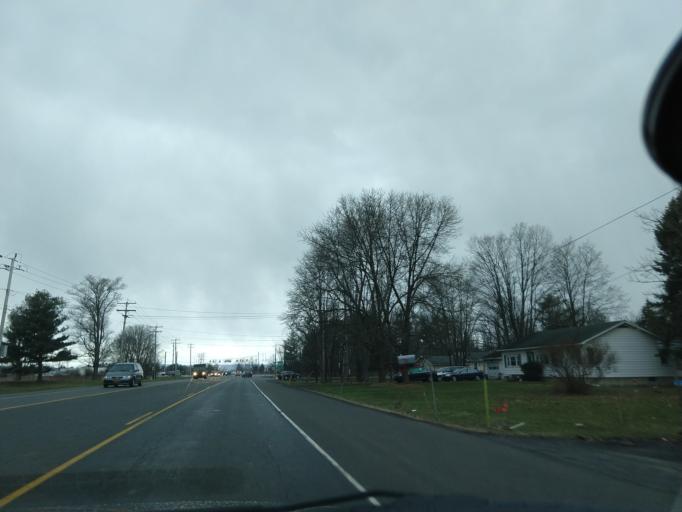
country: US
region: New York
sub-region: Tompkins County
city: Lansing
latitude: 42.4843
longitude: -76.4674
